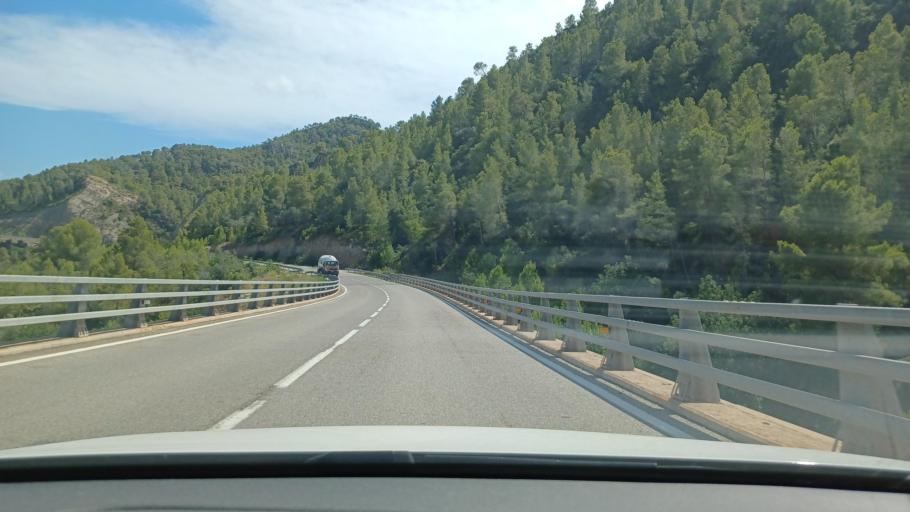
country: ES
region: Catalonia
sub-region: Provincia de Tarragona
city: Benifallet
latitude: 40.9531
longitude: 0.4471
